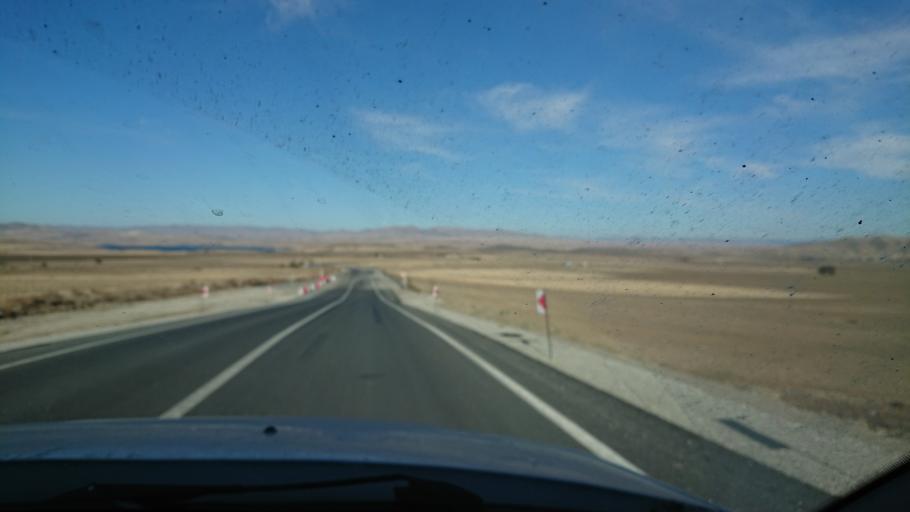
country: TR
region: Aksaray
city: Sariyahsi
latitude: 38.9996
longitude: 33.8542
